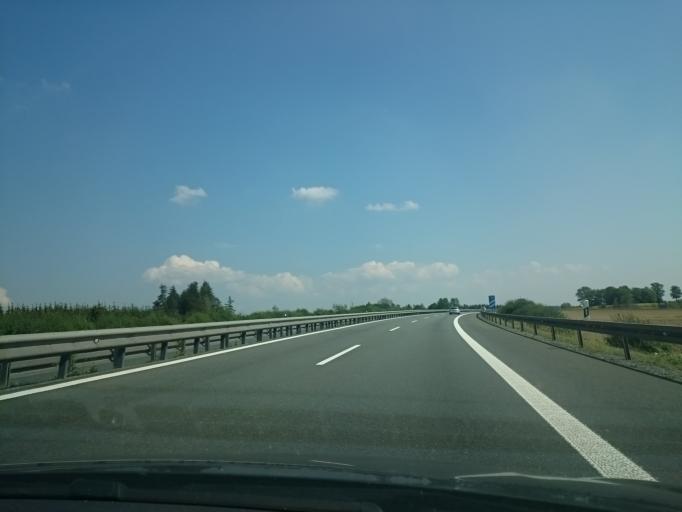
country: DE
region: Bavaria
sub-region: Upper Franconia
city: Topen
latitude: 50.3679
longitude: 11.8888
